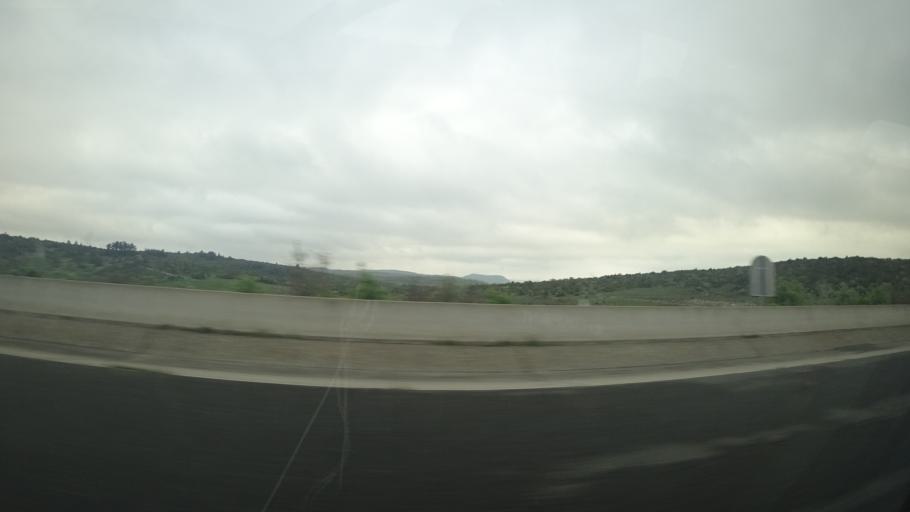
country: FR
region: Midi-Pyrenees
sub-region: Departement de l'Aveyron
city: Creissels
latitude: 44.0459
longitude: 3.0540
